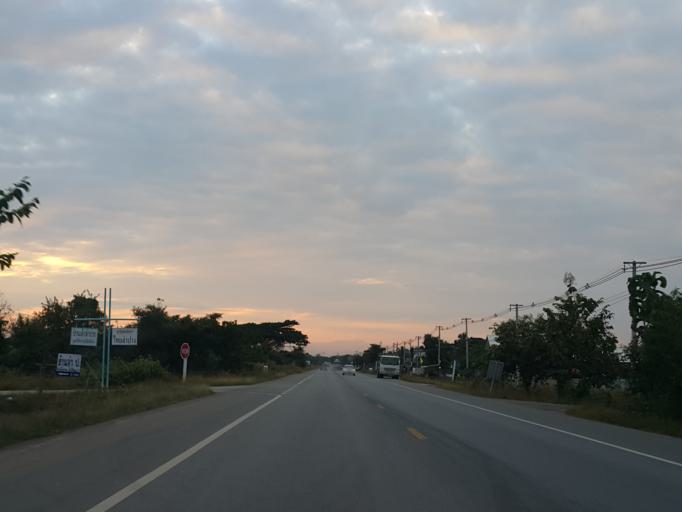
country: TH
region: Lampang
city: Lampang
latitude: 18.2513
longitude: 99.5123
